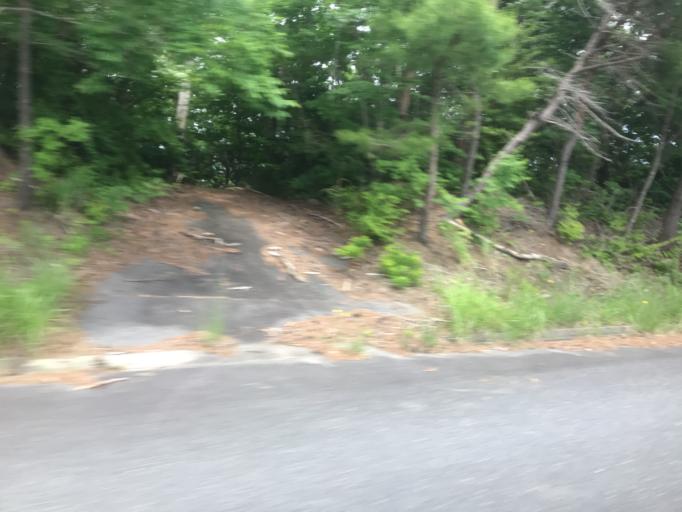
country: JP
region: Fukushima
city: Iwaki
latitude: 37.2477
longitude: 140.9915
